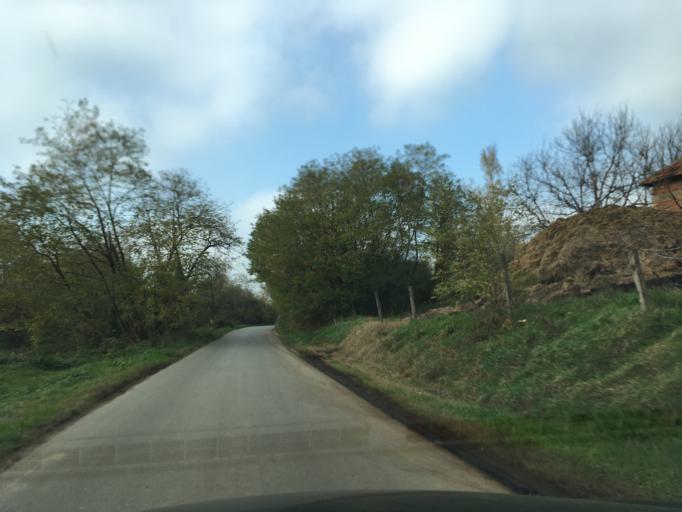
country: RS
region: Central Serbia
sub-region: Belgrade
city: Sopot
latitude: 44.4913
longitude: 20.5887
